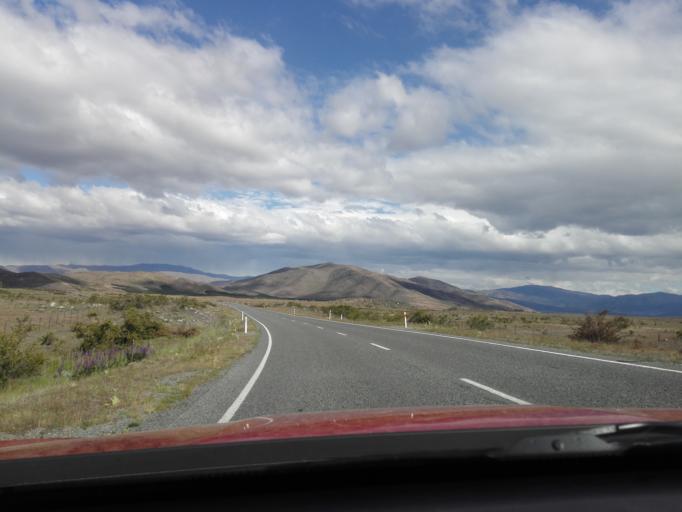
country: NZ
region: Canterbury
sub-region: Timaru District
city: Pleasant Point
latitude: -44.1995
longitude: 170.2493
